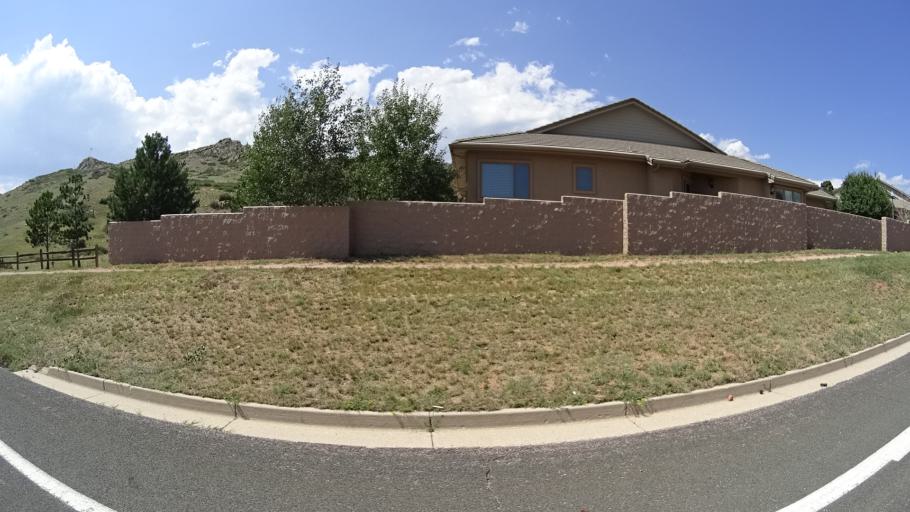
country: US
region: Colorado
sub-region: El Paso County
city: Manitou Springs
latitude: 38.9144
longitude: -104.8754
